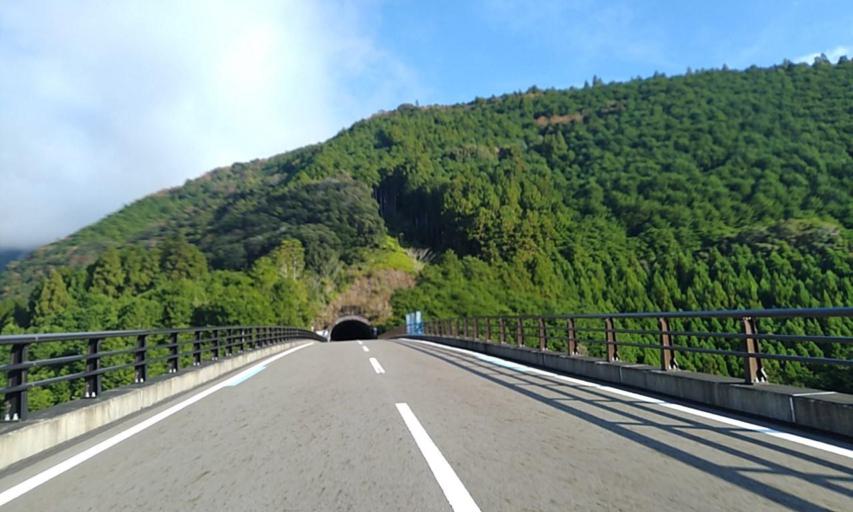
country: JP
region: Wakayama
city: Shingu
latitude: 33.8941
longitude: 135.8797
